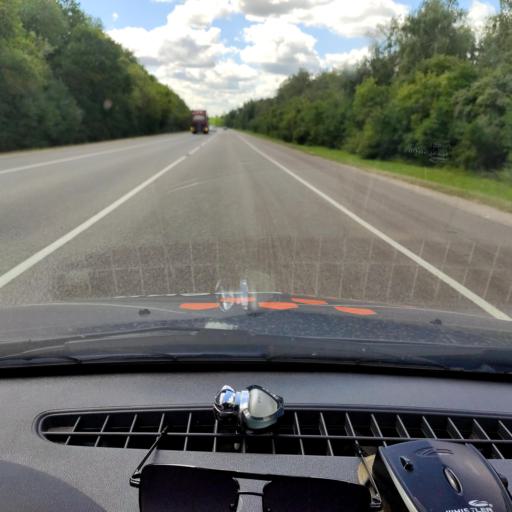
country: RU
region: Lipetsk
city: Borinskoye
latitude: 52.3723
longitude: 39.2104
